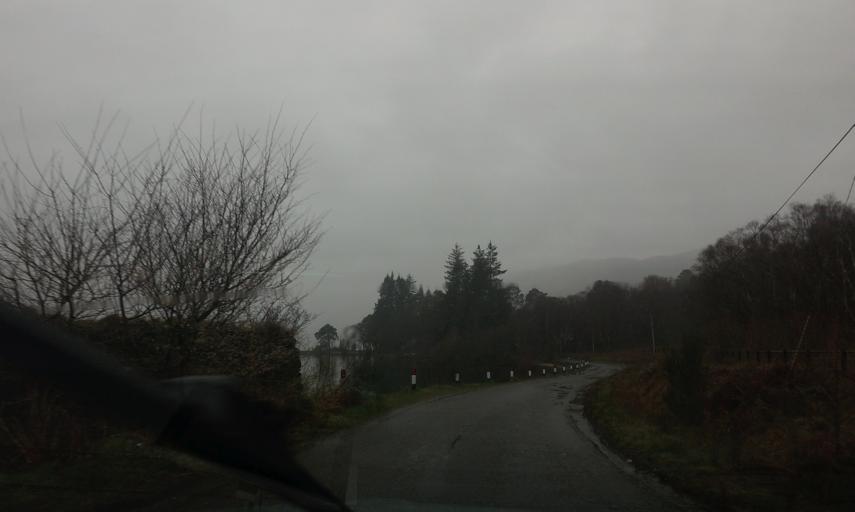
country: GB
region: Scotland
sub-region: West Dunbartonshire
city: Balloch
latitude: 56.1503
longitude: -4.6419
